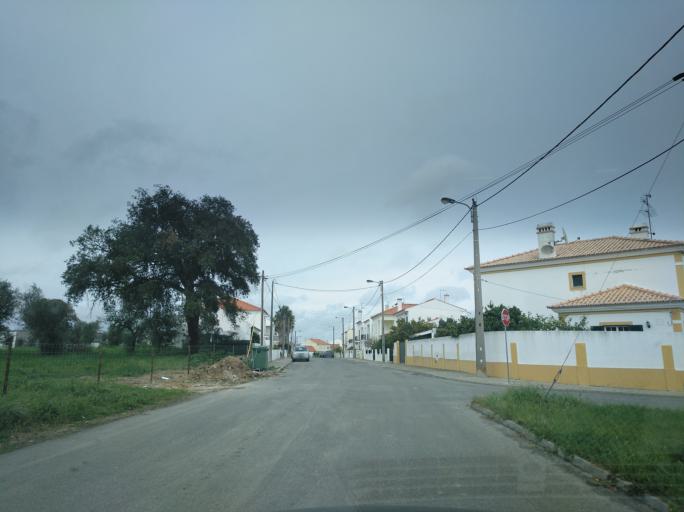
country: PT
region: Setubal
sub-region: Grandola
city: Grandola
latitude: 38.1801
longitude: -8.5724
